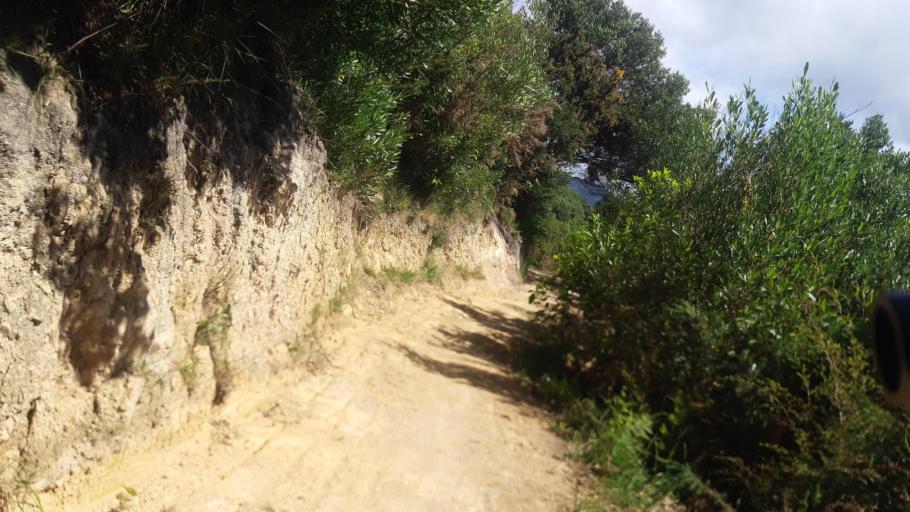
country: NZ
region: Marlborough
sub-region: Marlborough District
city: Picton
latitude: -41.2655
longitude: 174.0279
